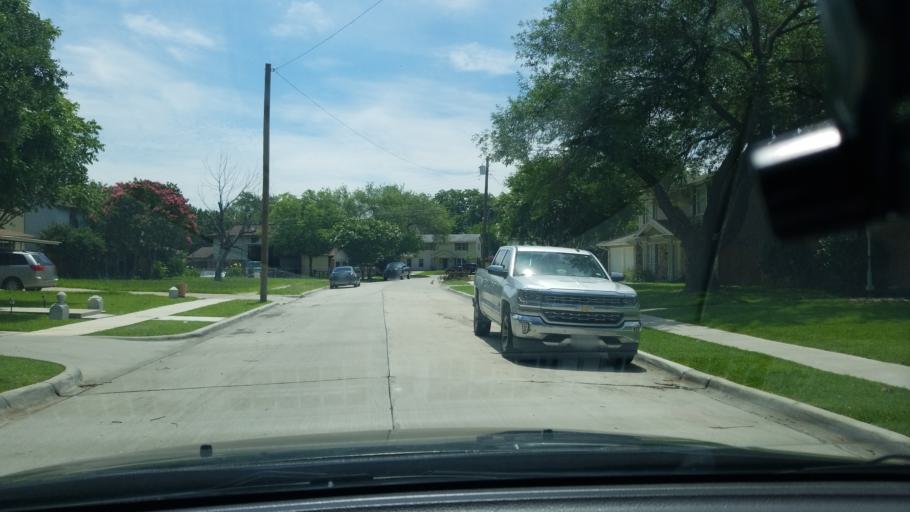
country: US
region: Texas
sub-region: Dallas County
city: Mesquite
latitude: 32.8057
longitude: -96.6550
